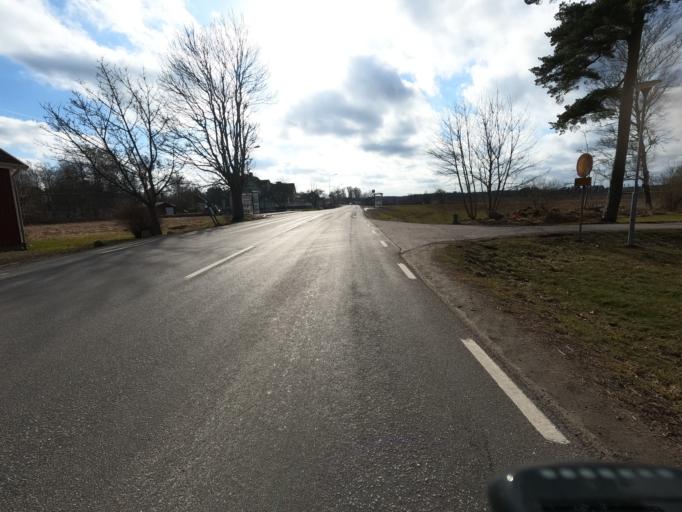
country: SE
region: Kronoberg
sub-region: Alvesta Kommun
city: Vislanda
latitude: 56.7410
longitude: 14.5461
